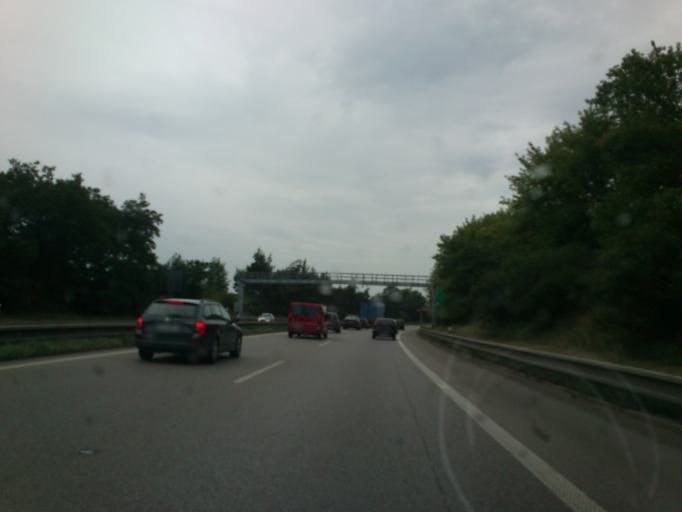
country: CZ
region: Central Bohemia
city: Brandys nad Labem-Stara Boleslav
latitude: 50.1956
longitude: 14.6926
